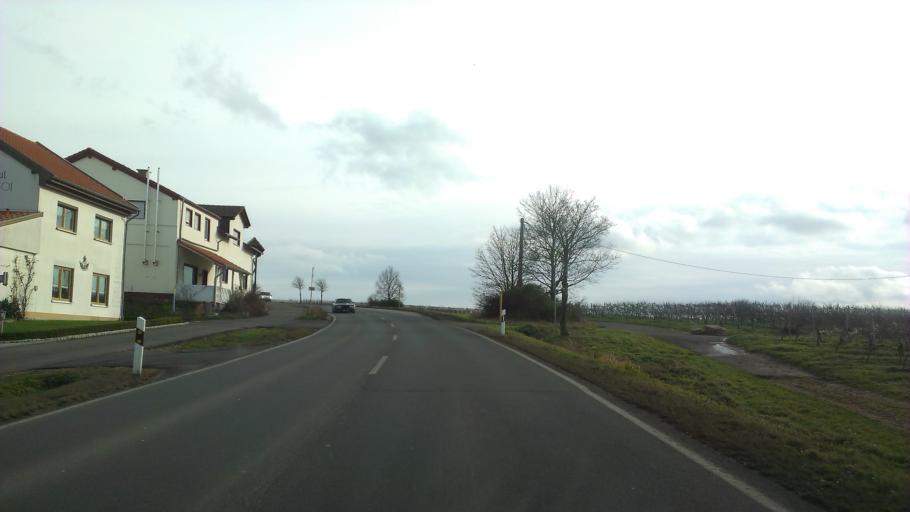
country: DE
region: Rheinland-Pfalz
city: Hackenheim
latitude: 49.8281
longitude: 7.8887
